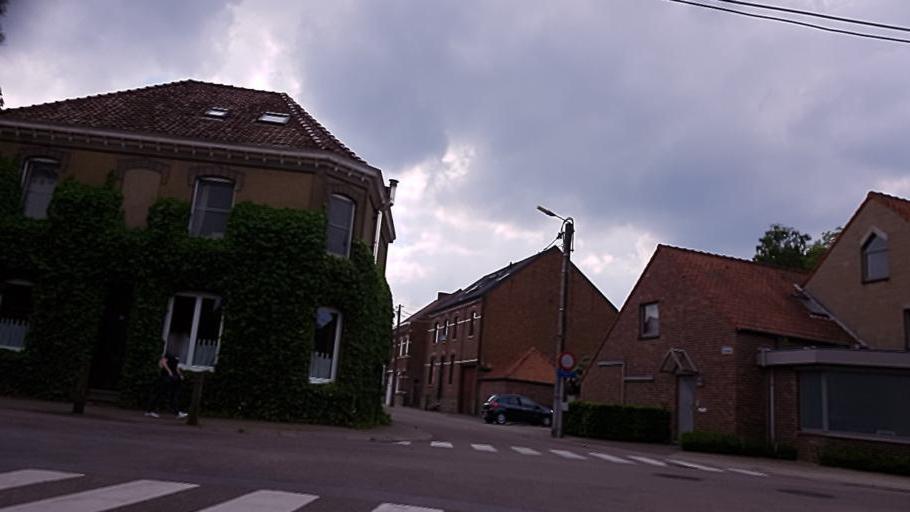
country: BE
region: Flanders
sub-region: Provincie Vlaams-Brabant
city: Bertem
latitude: 50.8478
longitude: 4.5852
